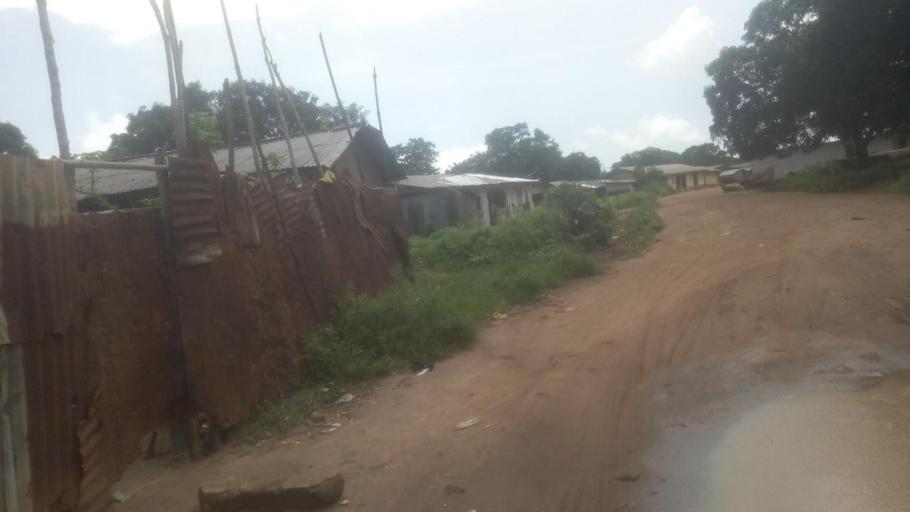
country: SL
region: Northern Province
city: Tintafor
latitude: 8.6307
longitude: -13.2167
